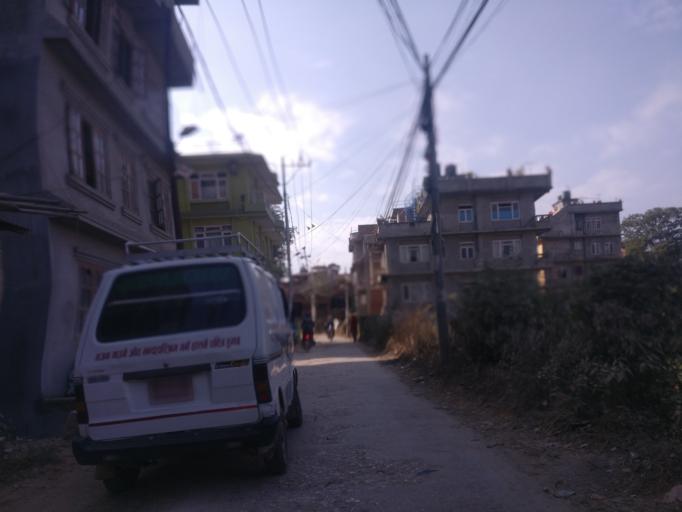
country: NP
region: Central Region
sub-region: Bagmati Zone
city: Patan
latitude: 27.6787
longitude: 85.3302
